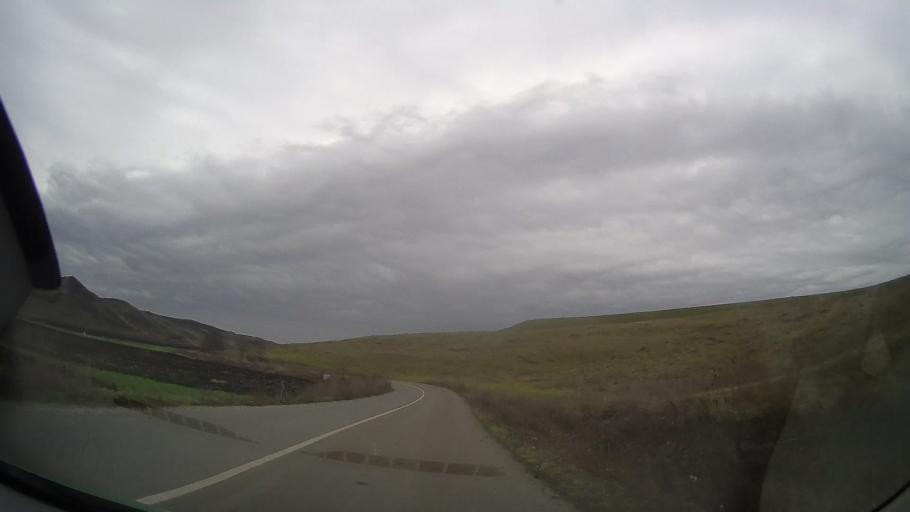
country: RO
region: Mures
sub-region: Comuna Craesti
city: Craiesti
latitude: 46.7847
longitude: 24.4252
